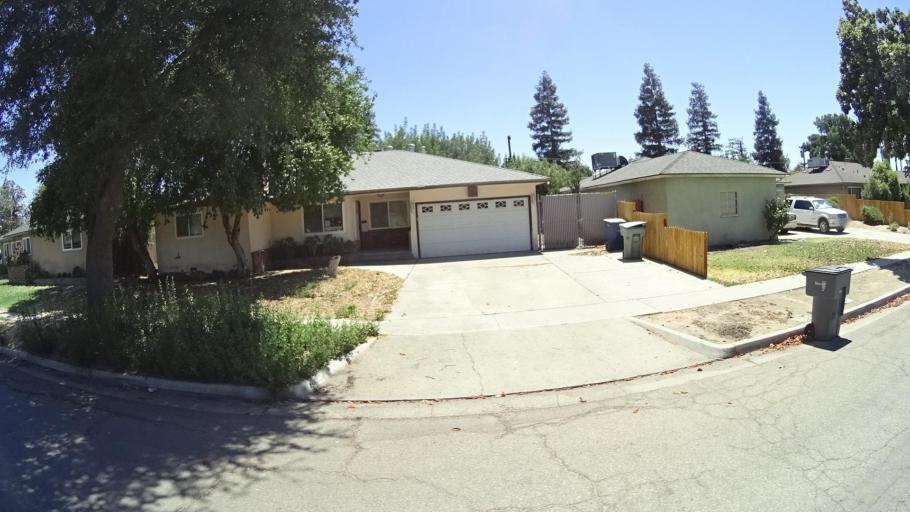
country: US
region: California
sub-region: Fresno County
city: Fresno
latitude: 36.8027
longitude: -119.7750
